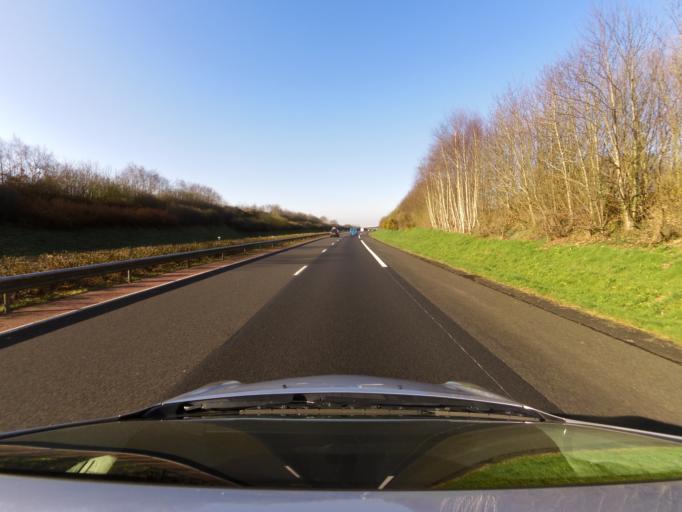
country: FR
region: Lower Normandy
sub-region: Departement de la Manche
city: Percy
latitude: 48.8824
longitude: -1.1461
